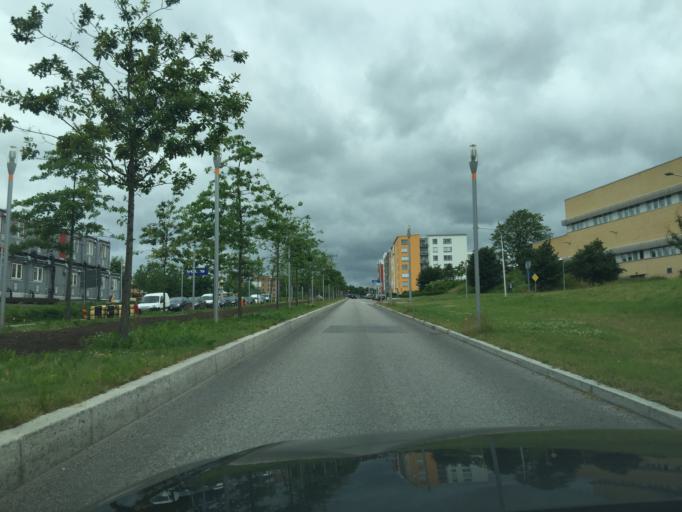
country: SE
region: Stockholm
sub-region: Stockholms Kommun
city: Kista
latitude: 59.4056
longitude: 17.9417
